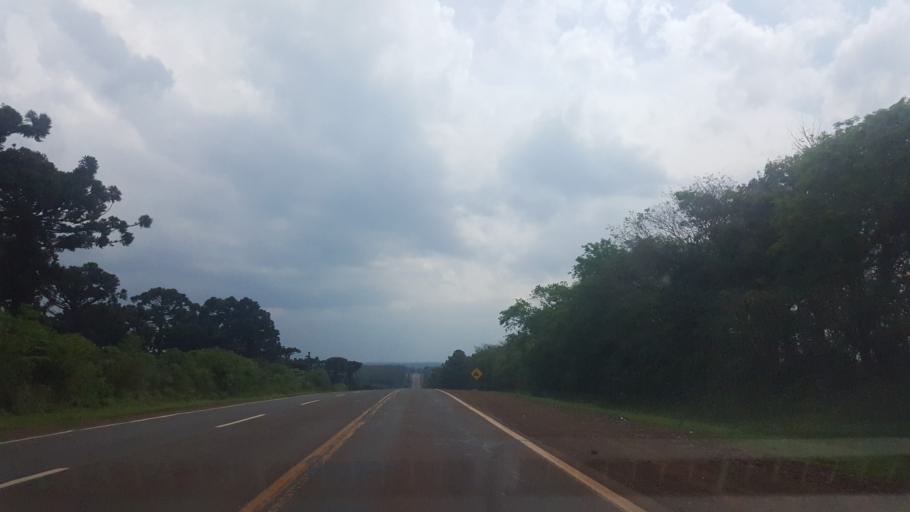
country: AR
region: Misiones
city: Jardin America
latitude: -27.1015
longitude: -55.3127
